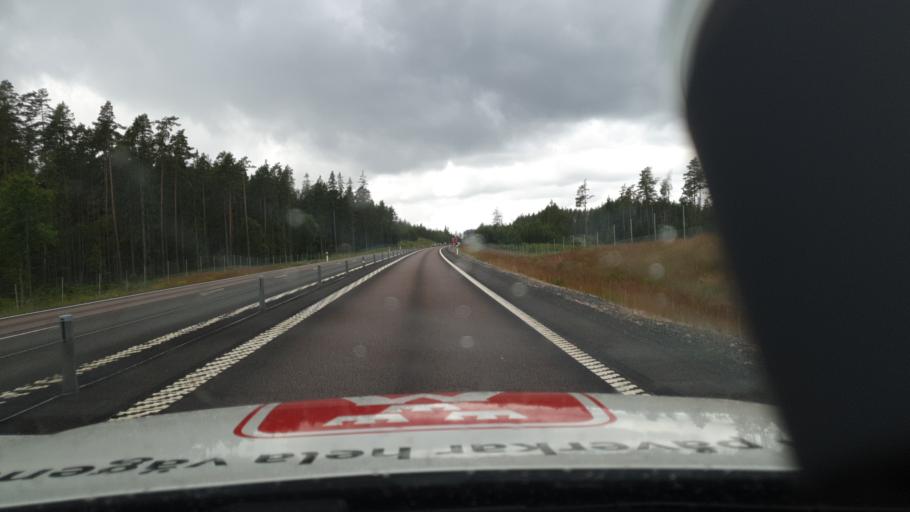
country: SE
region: Joenkoeping
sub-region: Mullsjo Kommun
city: Mullsjoe
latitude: 57.8669
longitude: 13.9686
